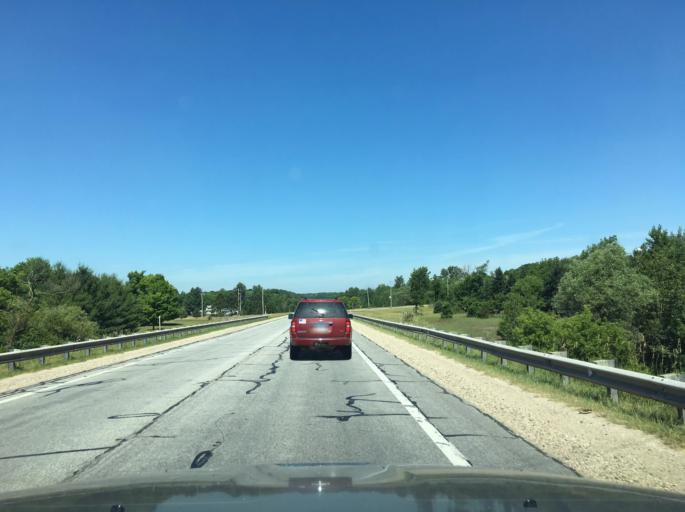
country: US
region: Michigan
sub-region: Osceola County
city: Reed City
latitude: 43.8786
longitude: -85.5009
